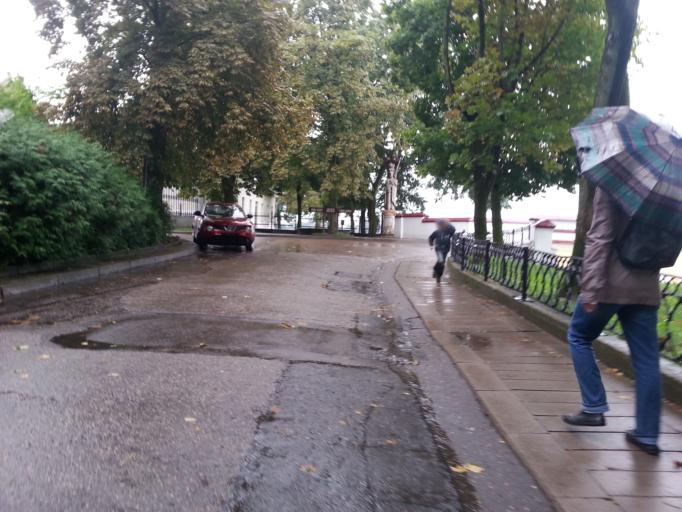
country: BY
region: Grodnenskaya
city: Hrodna
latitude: 53.6771
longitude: 23.8247
